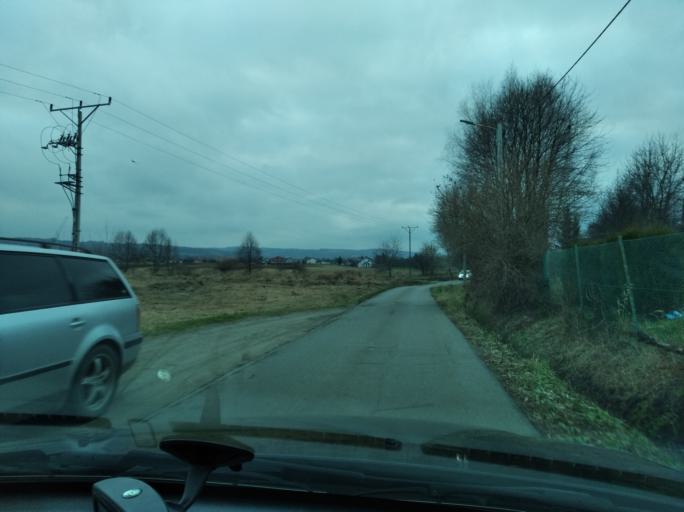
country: PL
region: Subcarpathian Voivodeship
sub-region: Powiat rzeszowski
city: Lutoryz
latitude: 49.9730
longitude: 21.9259
